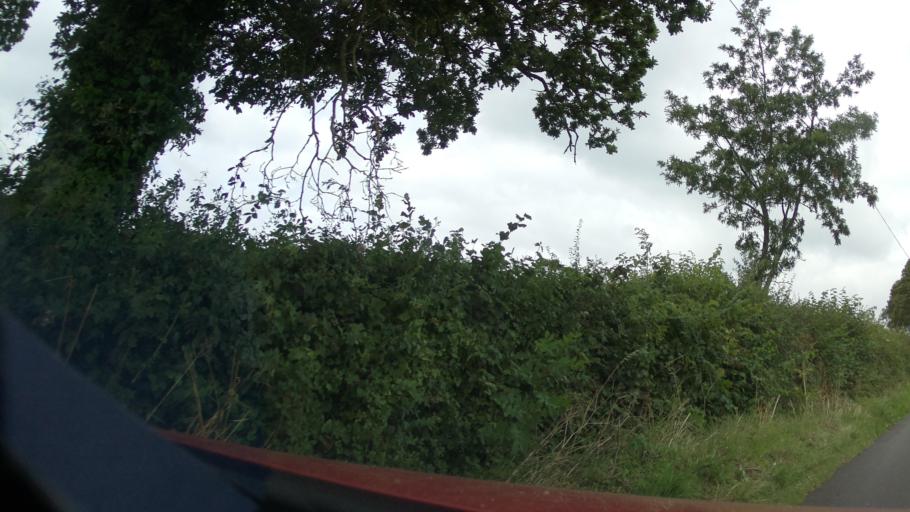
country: GB
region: England
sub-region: Dorset
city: Stalbridge
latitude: 50.9554
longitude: -2.3987
